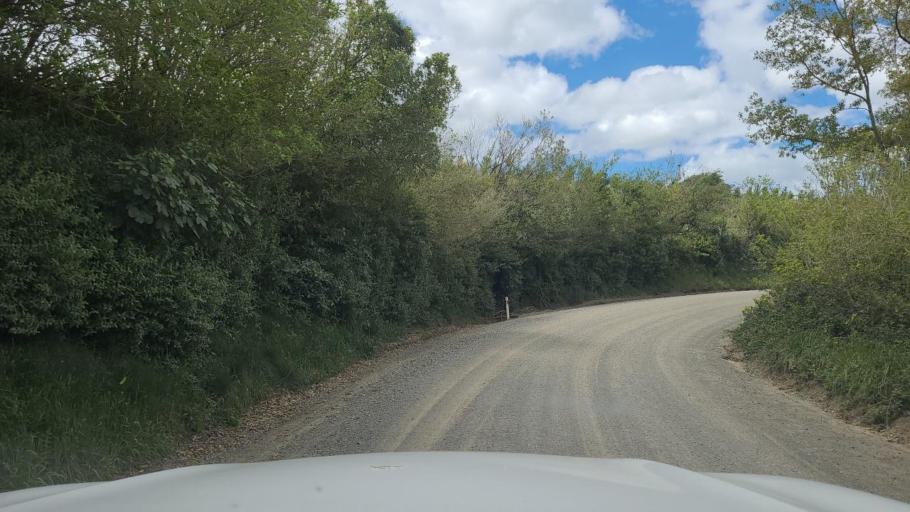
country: NZ
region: Hawke's Bay
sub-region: Napier City
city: Napier
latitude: -39.2506
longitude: 176.7302
